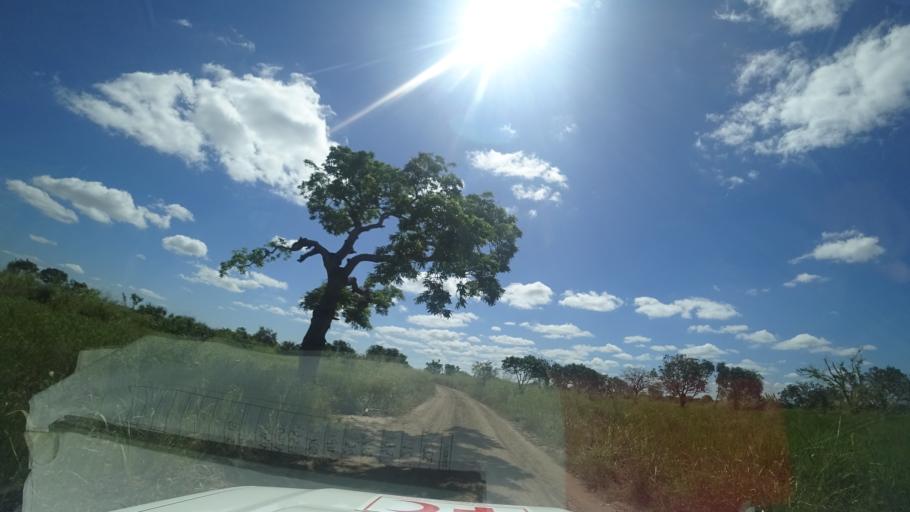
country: MZ
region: Sofala
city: Dondo
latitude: -19.4636
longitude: 34.5952
